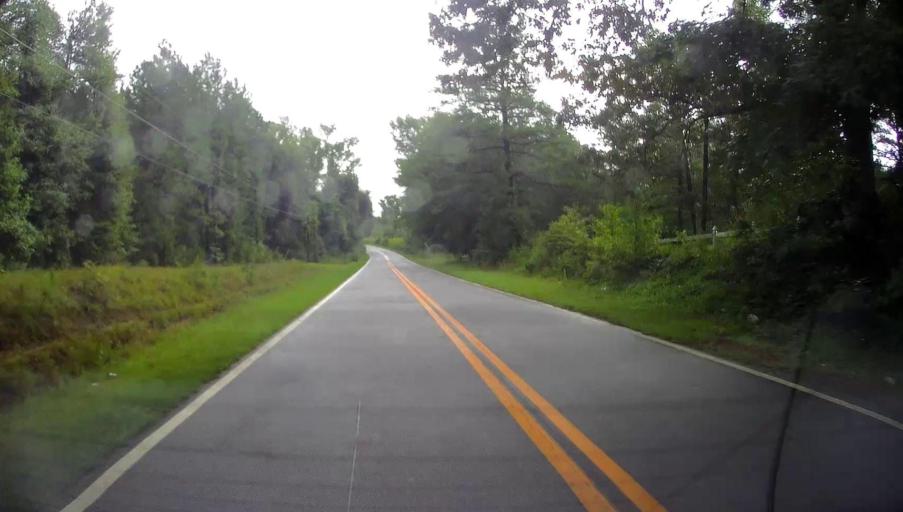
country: US
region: Georgia
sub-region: Bibb County
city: West Point
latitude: 32.7897
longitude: -83.7642
